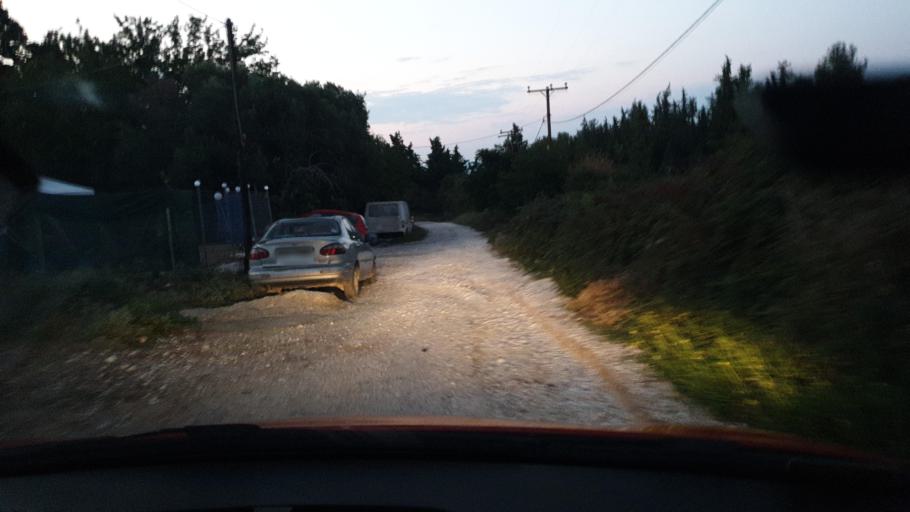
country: GR
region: Central Macedonia
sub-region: Nomos Thessalonikis
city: Agia Triada
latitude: 40.5031
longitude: 22.8354
